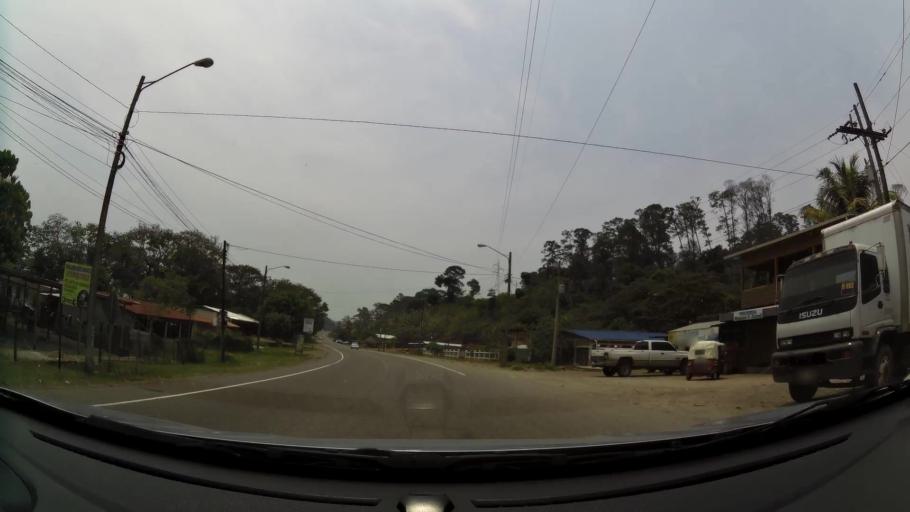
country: HN
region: Cortes
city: La Guama
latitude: 14.8897
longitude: -87.9389
